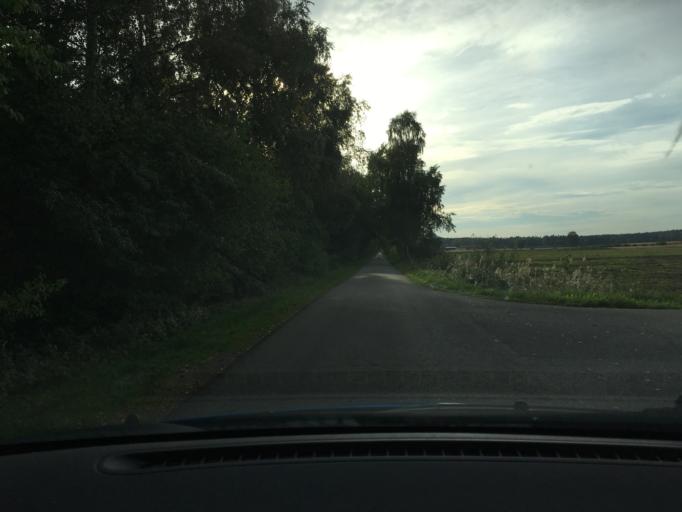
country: DE
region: Lower Saxony
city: Wietzendorf
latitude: 52.8905
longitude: 9.9360
